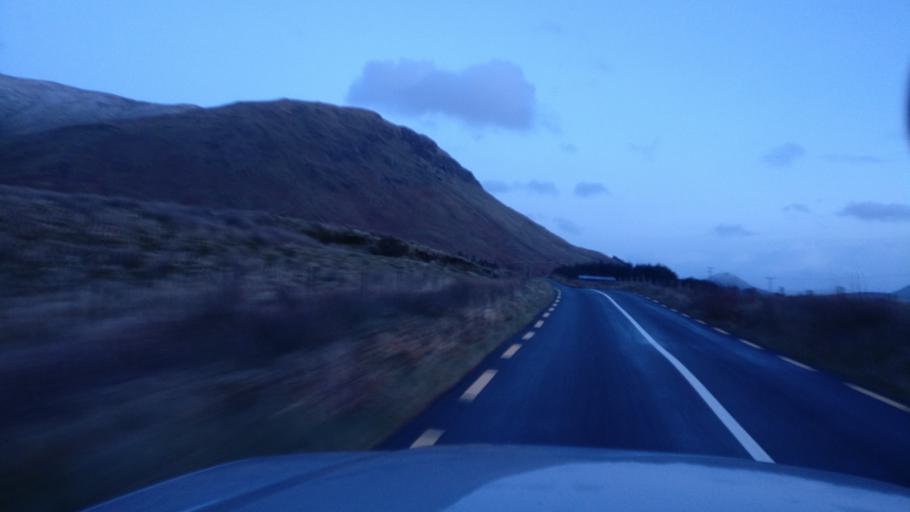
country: IE
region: Connaught
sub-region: Maigh Eo
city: Westport
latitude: 53.5496
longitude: -9.6317
